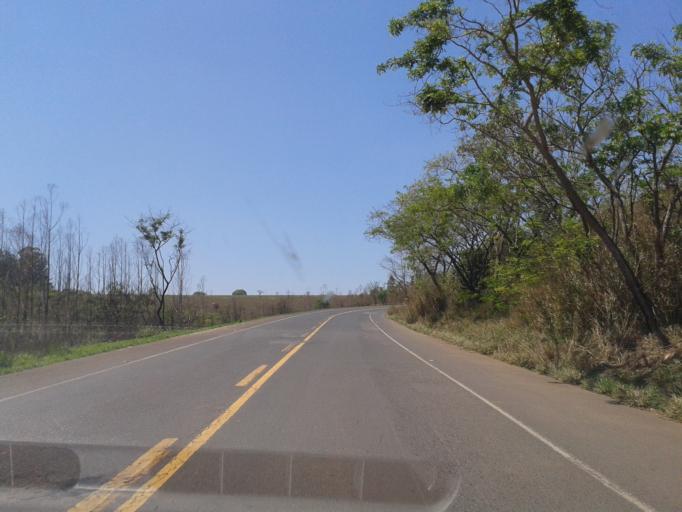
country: BR
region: Minas Gerais
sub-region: Araxa
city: Araxa
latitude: -19.4600
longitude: -47.1714
